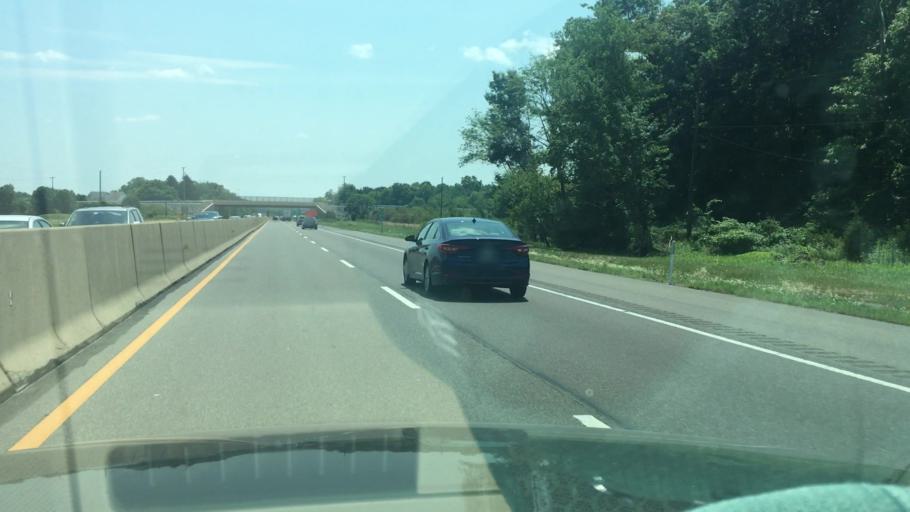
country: US
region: Pennsylvania
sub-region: Bucks County
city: Spinnerstown
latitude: 40.4459
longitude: -75.4328
